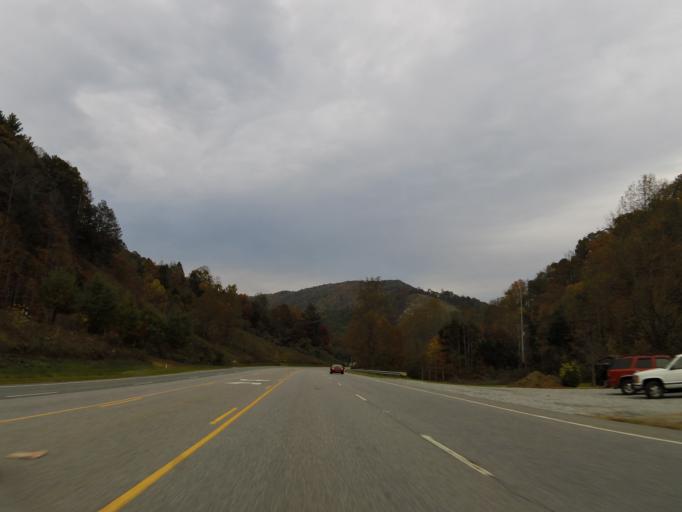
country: US
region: North Carolina
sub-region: Caldwell County
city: Lenoir
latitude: 36.0265
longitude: -81.5832
